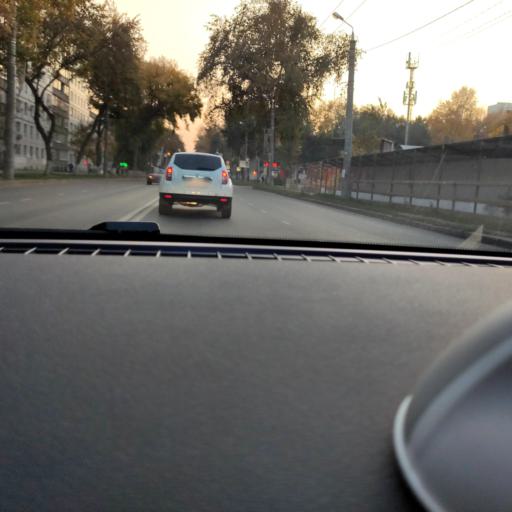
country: RU
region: Samara
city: Petra-Dubrava
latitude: 53.2289
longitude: 50.2667
